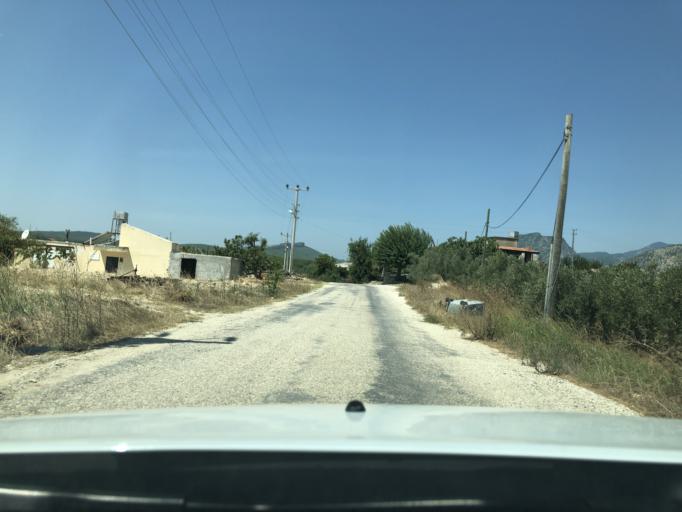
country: TR
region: Antalya
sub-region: Manavgat
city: Kizilagac
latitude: 36.8569
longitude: 31.5575
